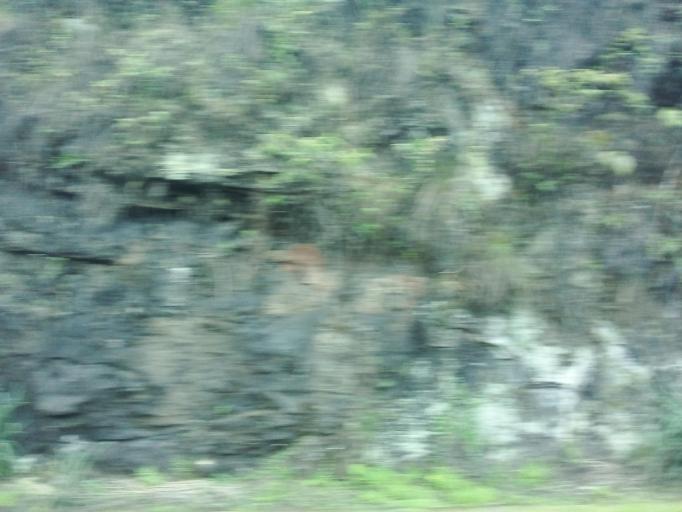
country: BR
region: Minas Gerais
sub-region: Joao Monlevade
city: Joao Monlevade
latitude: -19.8256
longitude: -43.1199
